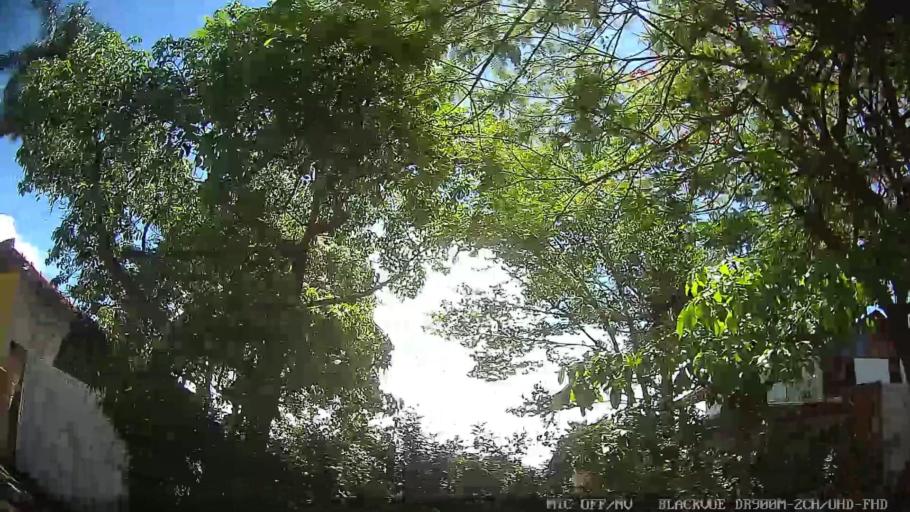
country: BR
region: Sao Paulo
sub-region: Pedreira
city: Pedreira
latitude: -22.7500
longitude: -46.9217
